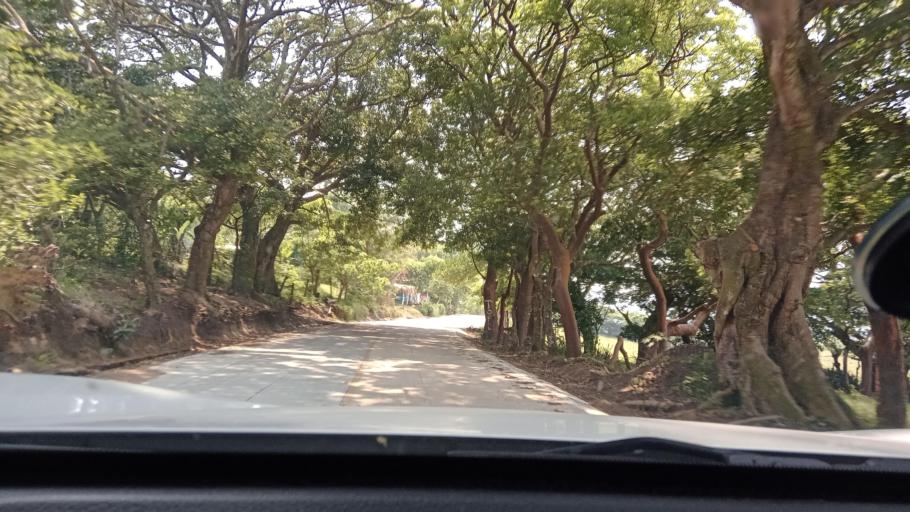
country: MX
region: Veracruz
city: Catemaco
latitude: 18.5578
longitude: -95.0147
